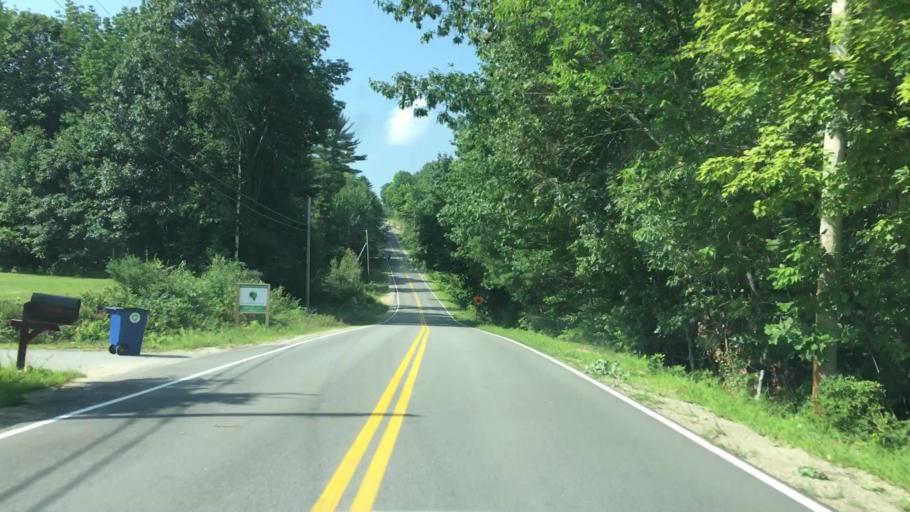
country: US
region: Maine
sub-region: Androscoggin County
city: Poland
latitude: 43.9828
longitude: -70.3990
